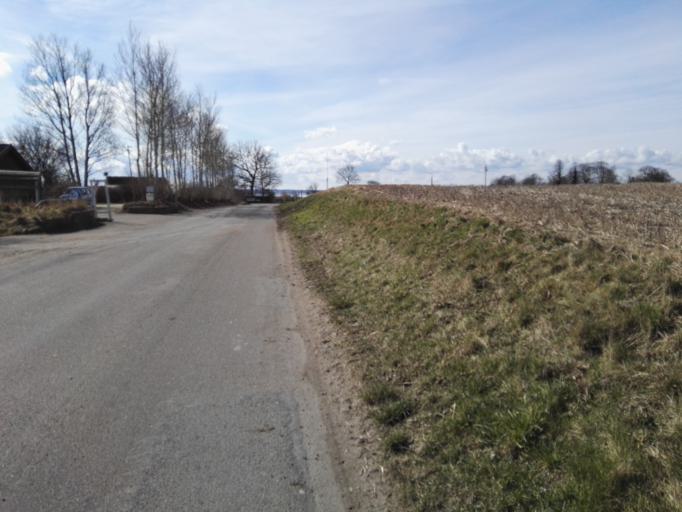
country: DK
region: Zealand
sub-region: Lejre Kommune
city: Ejby
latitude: 55.7675
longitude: 11.8140
